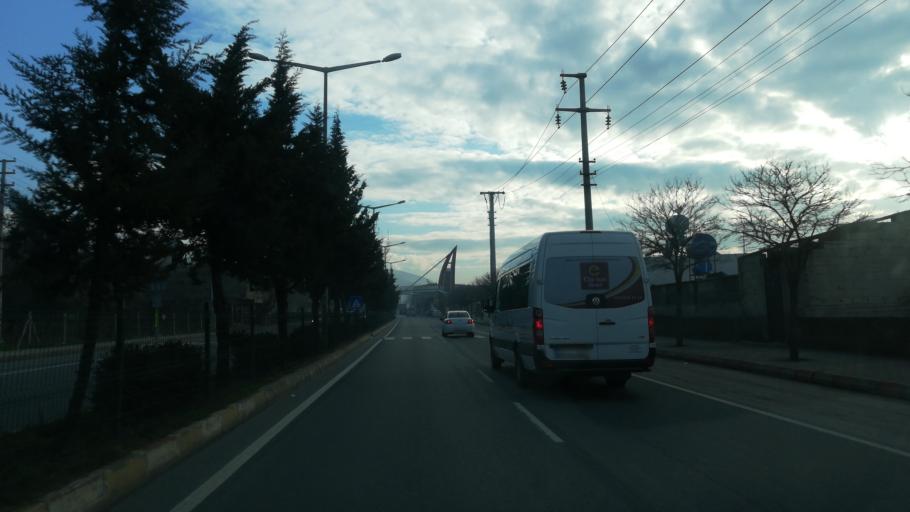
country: TR
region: Kahramanmaras
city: Kahramanmaras
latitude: 37.5947
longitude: 36.9089
